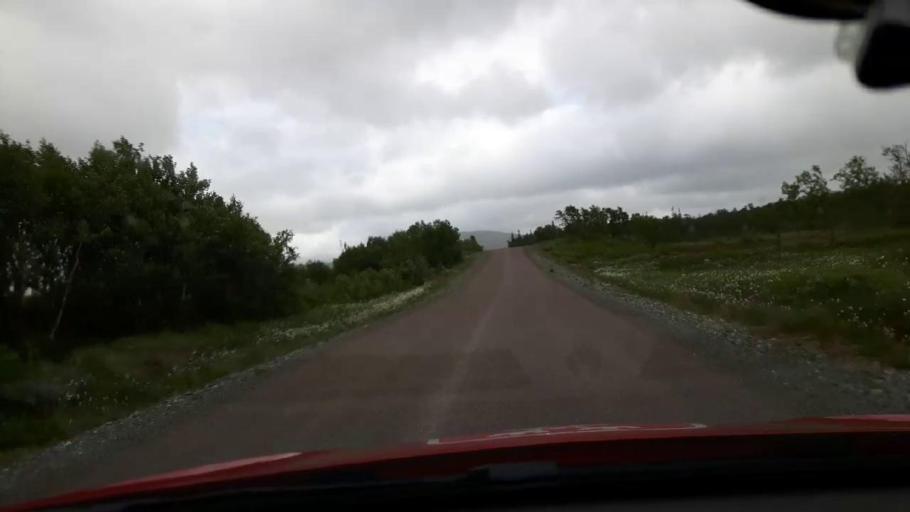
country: SE
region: Jaemtland
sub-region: Are Kommun
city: Are
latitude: 63.2421
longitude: 12.4302
